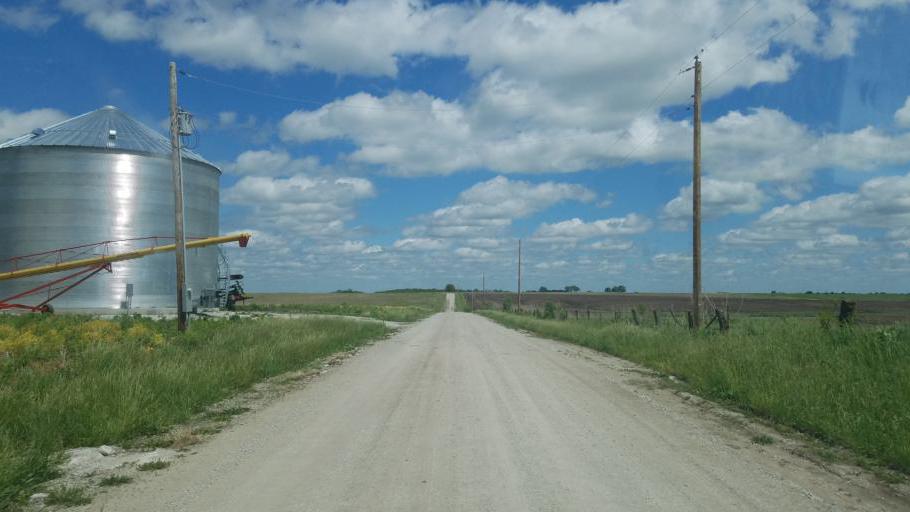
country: US
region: Iowa
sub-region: Decatur County
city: Lamoni
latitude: 40.5005
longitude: -93.9932
